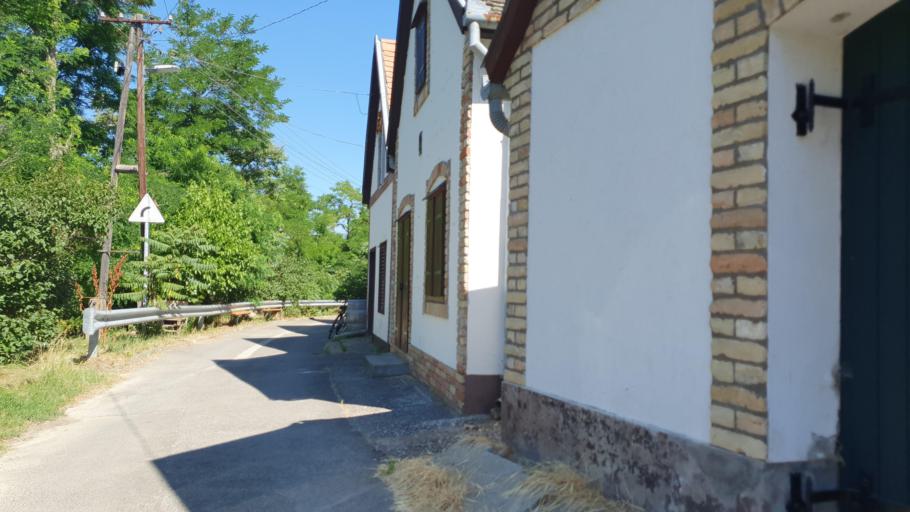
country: HU
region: Bacs-Kiskun
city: Hajos
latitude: 46.3869
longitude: 19.1485
